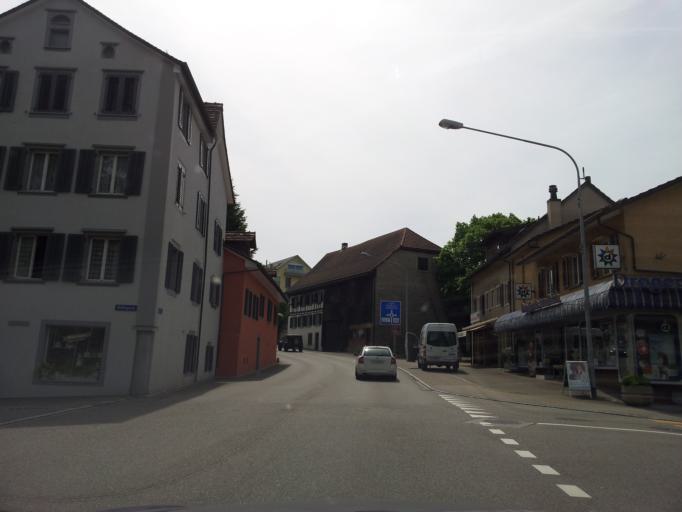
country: CH
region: Aargau
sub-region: Bezirk Baden
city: Wurenlos
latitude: 47.4421
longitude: 8.3628
